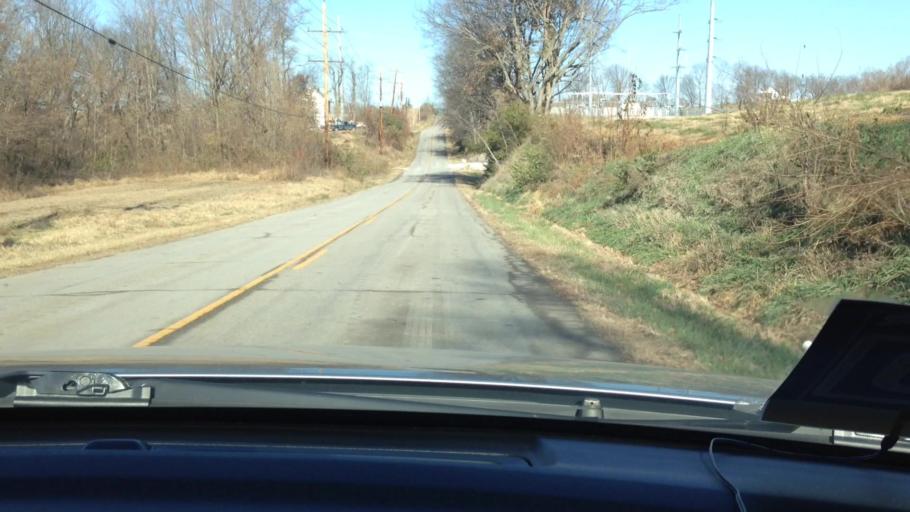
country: US
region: Missouri
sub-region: Platte County
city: Weston
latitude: 39.4252
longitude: -94.9007
